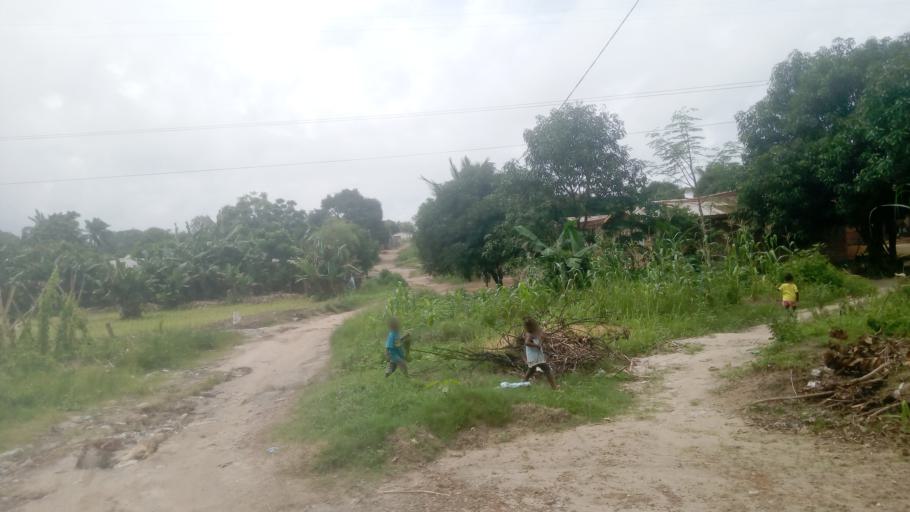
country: SL
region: Northern Province
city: Lunsar
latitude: 8.6918
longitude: -12.5398
